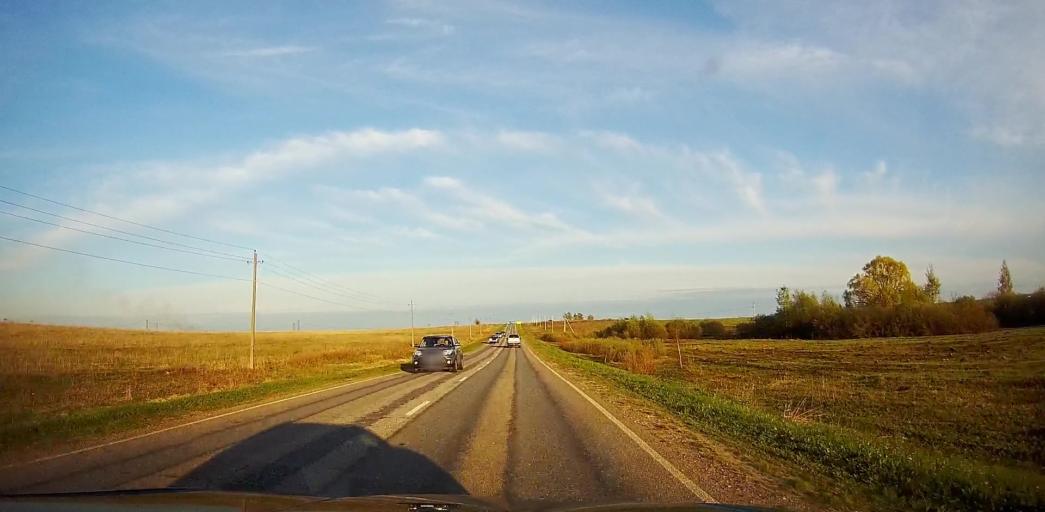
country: RU
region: Moskovskaya
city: Meshcherino
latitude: 55.2709
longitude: 38.2393
